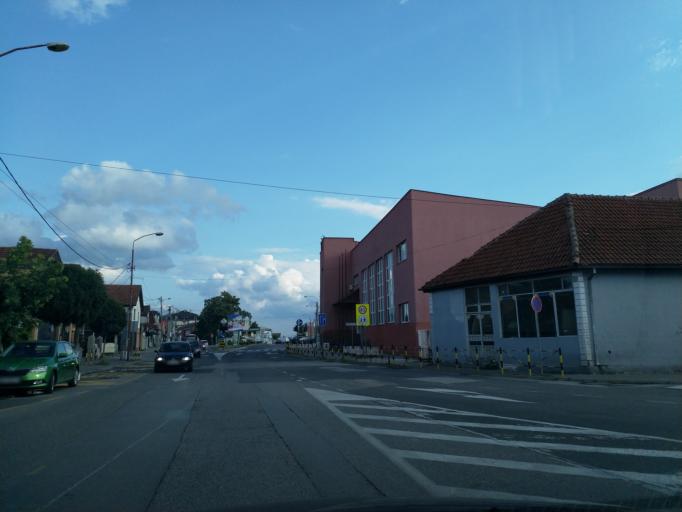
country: RS
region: Central Serbia
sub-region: Pomoravski Okrug
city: Paracin
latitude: 43.8553
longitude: 21.4126
